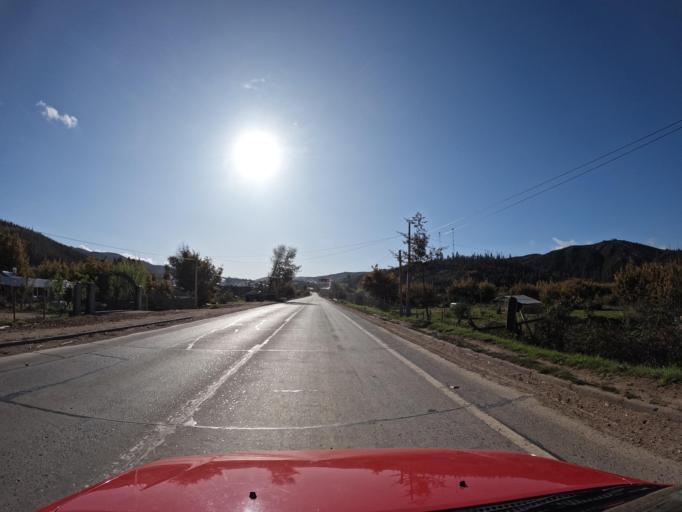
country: CL
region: Maule
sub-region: Provincia de Talca
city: Constitucion
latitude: -35.4566
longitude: -72.2666
